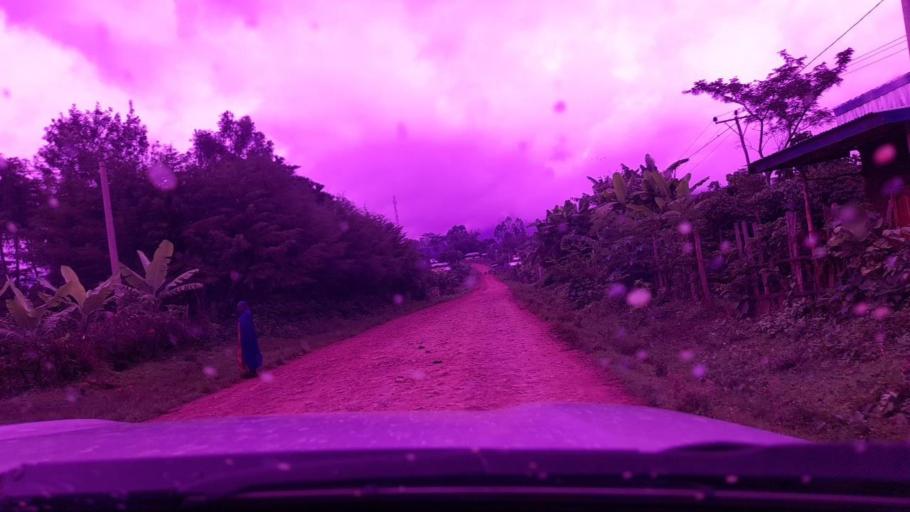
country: ET
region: Southern Nations, Nationalities, and People's Region
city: Bonga
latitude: 7.5515
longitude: 35.8617
